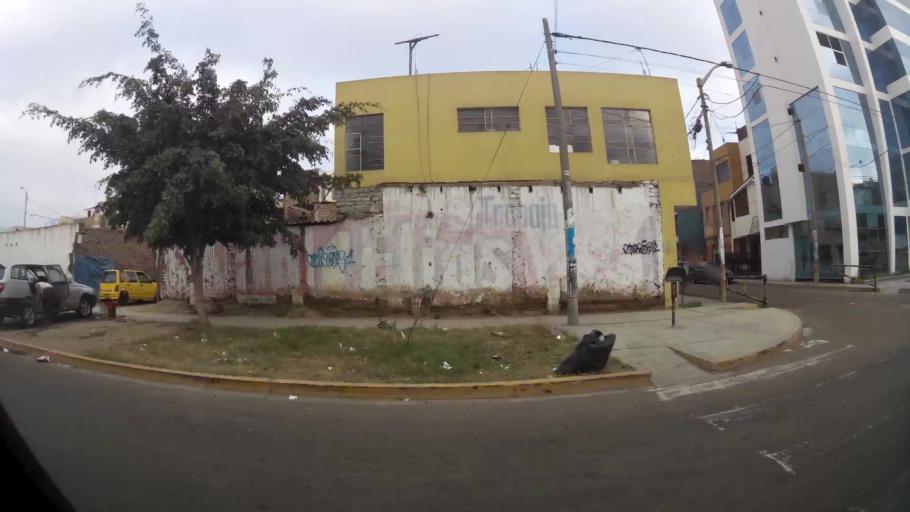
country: PE
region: La Libertad
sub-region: Provincia de Trujillo
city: Trujillo
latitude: -8.1001
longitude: -79.0214
